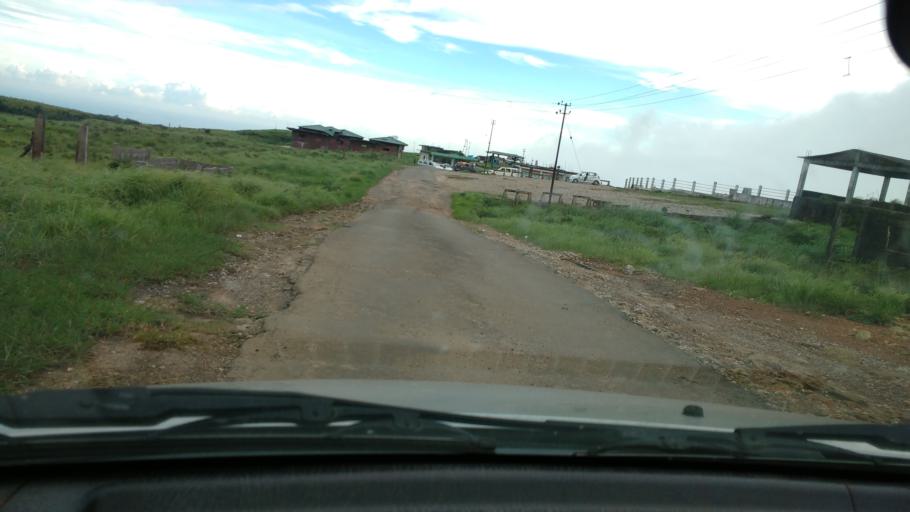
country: IN
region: Meghalaya
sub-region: East Khasi Hills
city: Cherrapunji
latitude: 25.2729
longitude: 91.6910
